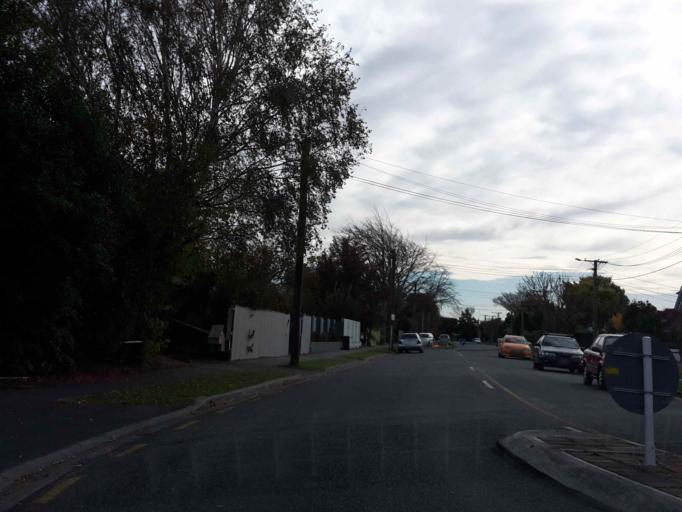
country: NZ
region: Canterbury
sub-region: Christchurch City
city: Christchurch
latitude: -43.5681
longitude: 172.6220
